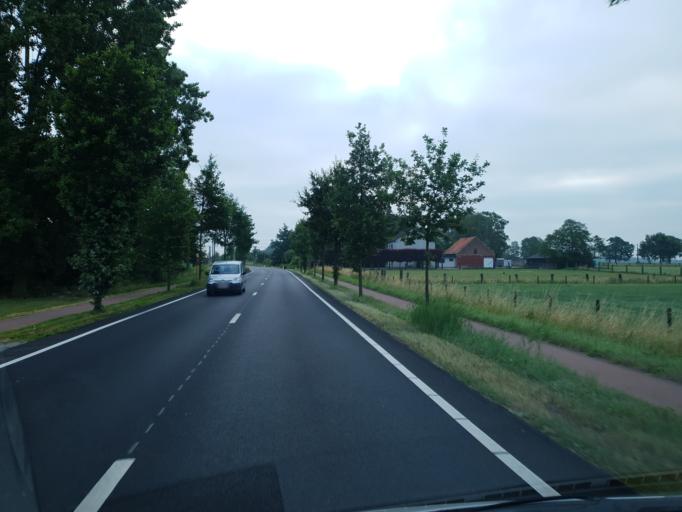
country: BE
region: Flanders
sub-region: Provincie Antwerpen
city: Rijkevorsel
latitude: 51.3622
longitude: 4.7023
